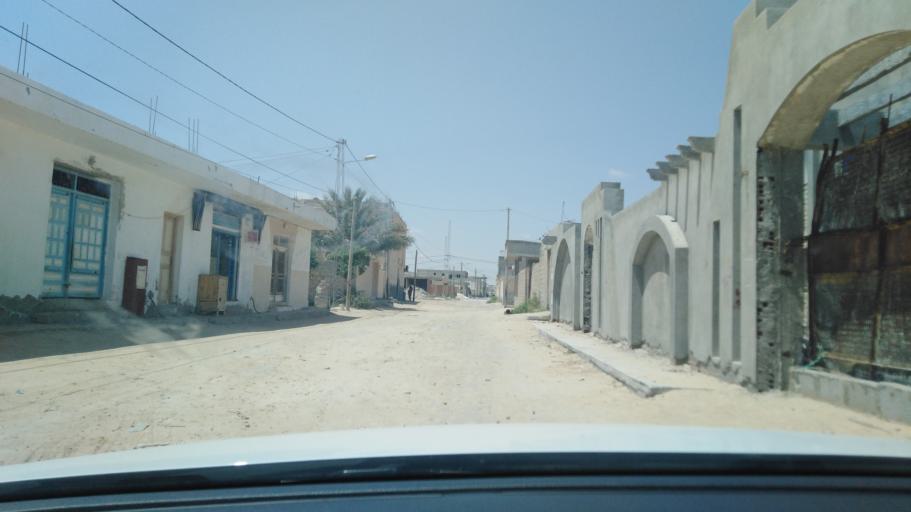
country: TN
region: Qabis
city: Gabes
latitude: 33.9452
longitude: 10.0742
